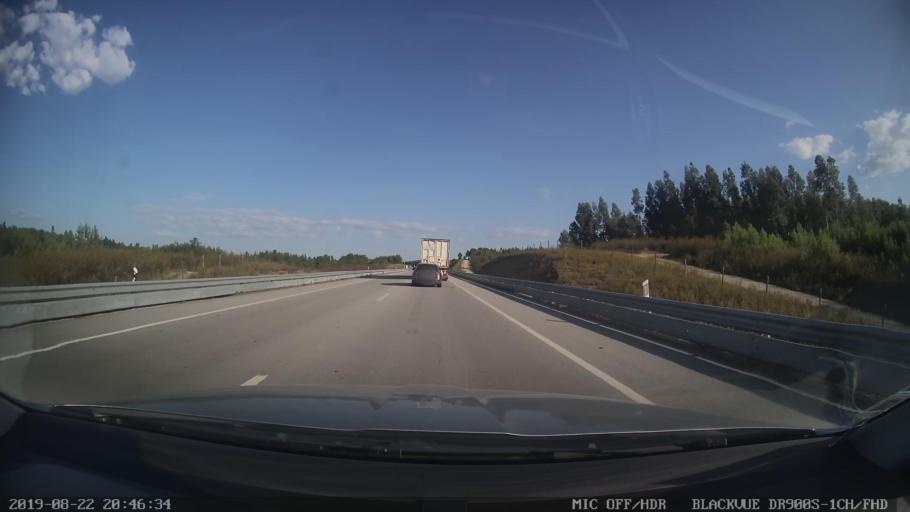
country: PT
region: Castelo Branco
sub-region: Proenca-A-Nova
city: Proenca-a-Nova
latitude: 39.7278
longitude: -7.8778
